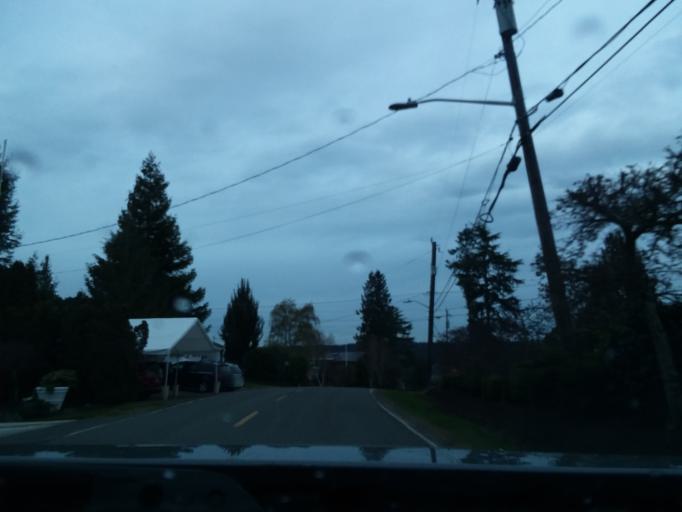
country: US
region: Washington
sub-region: King County
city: Shoreline
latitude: 47.6997
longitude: -122.3928
